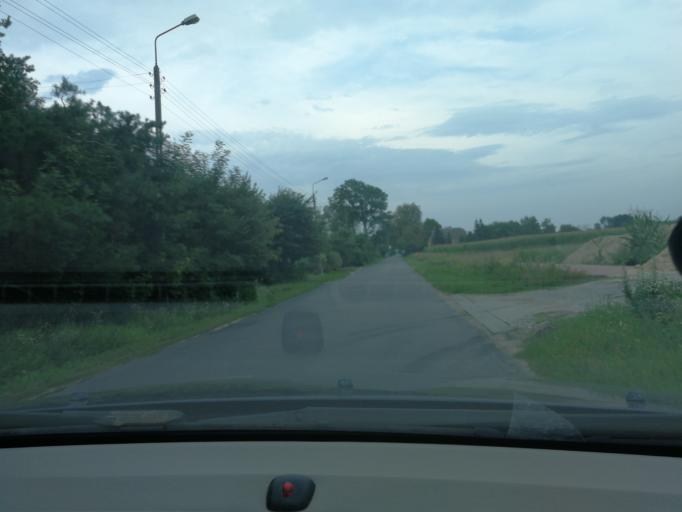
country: PL
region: Masovian Voivodeship
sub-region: Powiat grodziski
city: Grodzisk Mazowiecki
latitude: 52.1269
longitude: 20.6093
